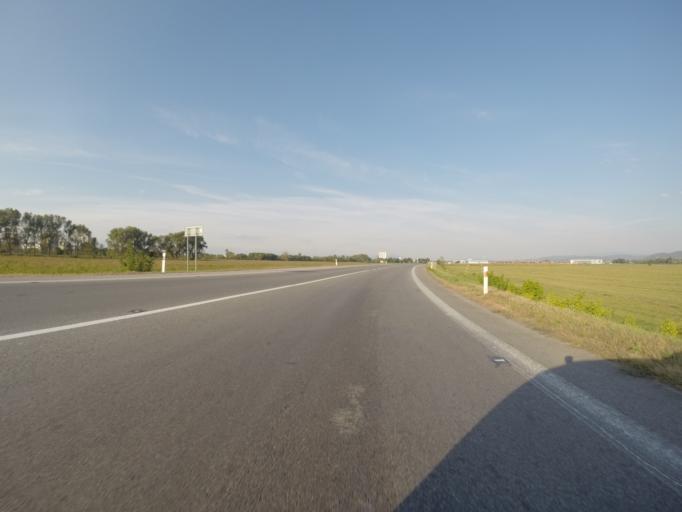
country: SK
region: Nitriansky
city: Banovce nad Bebravou
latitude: 48.5545
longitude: 18.1882
